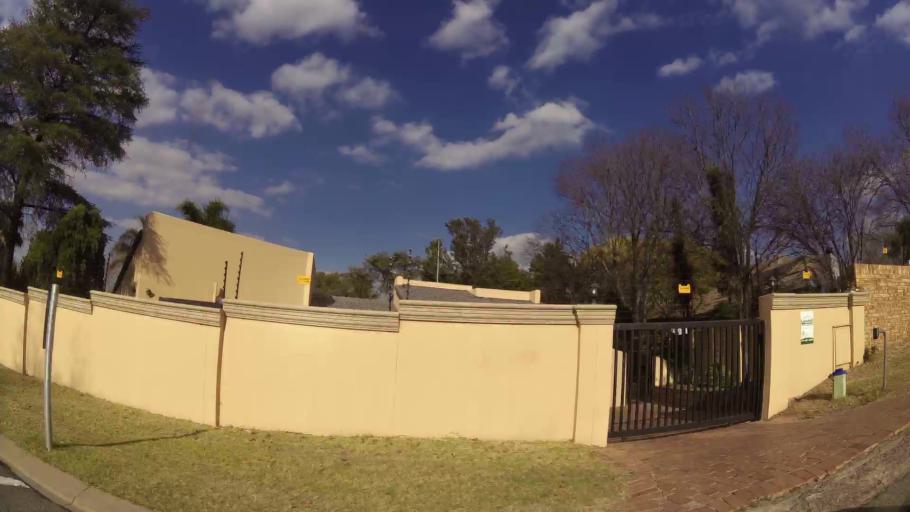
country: ZA
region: Gauteng
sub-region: City of Johannesburg Metropolitan Municipality
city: Diepsloot
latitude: -26.0092
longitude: 28.0236
